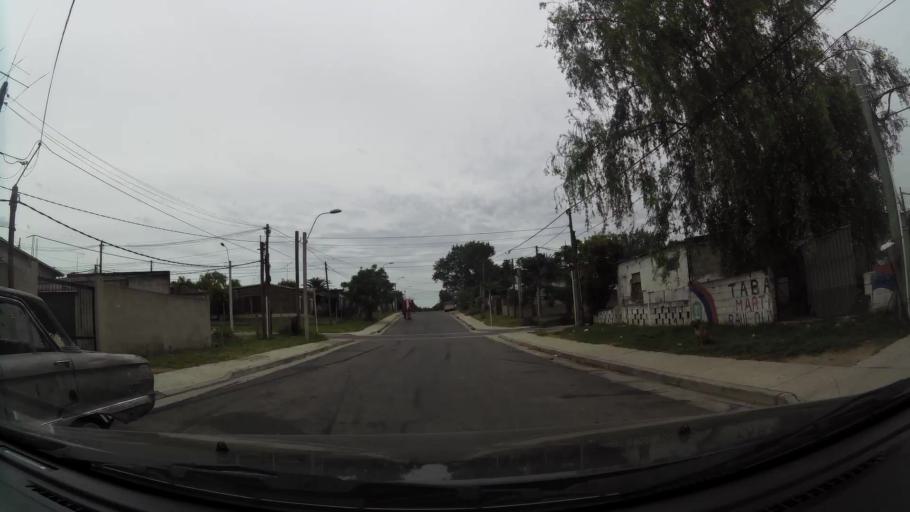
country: UY
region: Canelones
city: Las Piedras
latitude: -34.7310
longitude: -56.2084
